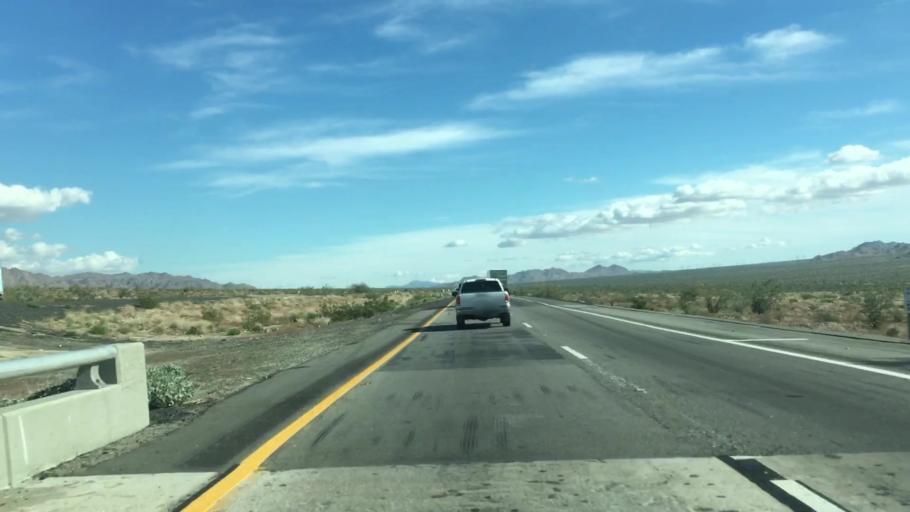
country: US
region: California
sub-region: Riverside County
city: Mecca
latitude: 33.6636
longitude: -115.8637
